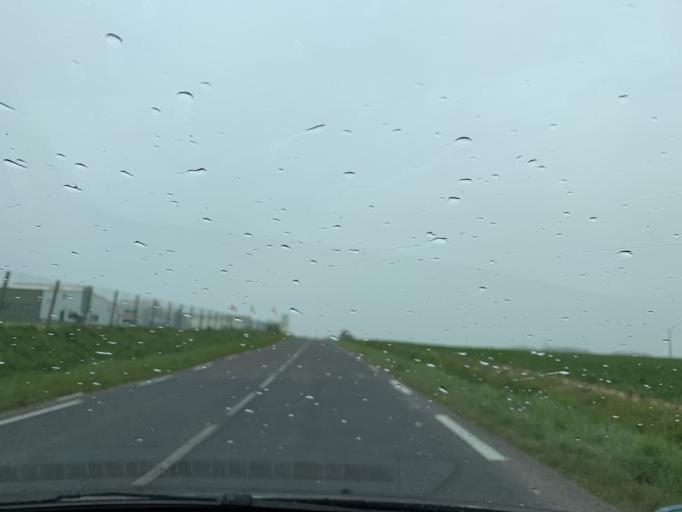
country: FR
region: Haute-Normandie
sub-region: Departement de la Seine-Maritime
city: Cany-Barville
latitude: 49.7869
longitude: 0.6570
